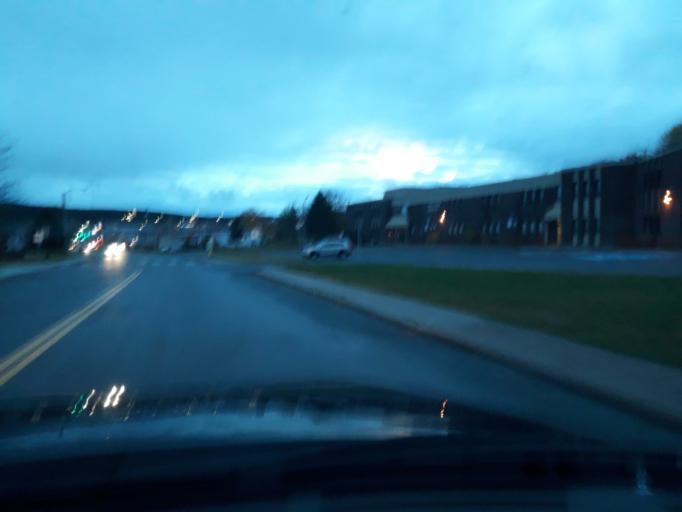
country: CA
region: Newfoundland and Labrador
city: St. John's
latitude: 47.5648
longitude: -52.7540
